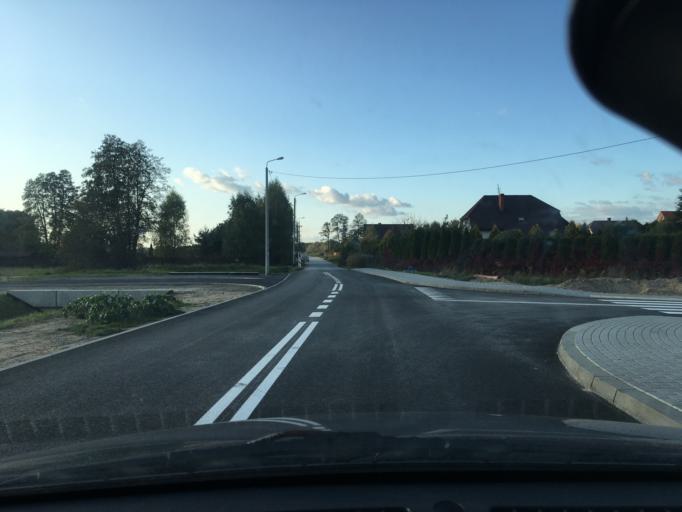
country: PL
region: Masovian Voivodeship
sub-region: Powiat piaseczynski
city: Lesznowola
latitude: 52.0473
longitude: 20.9309
